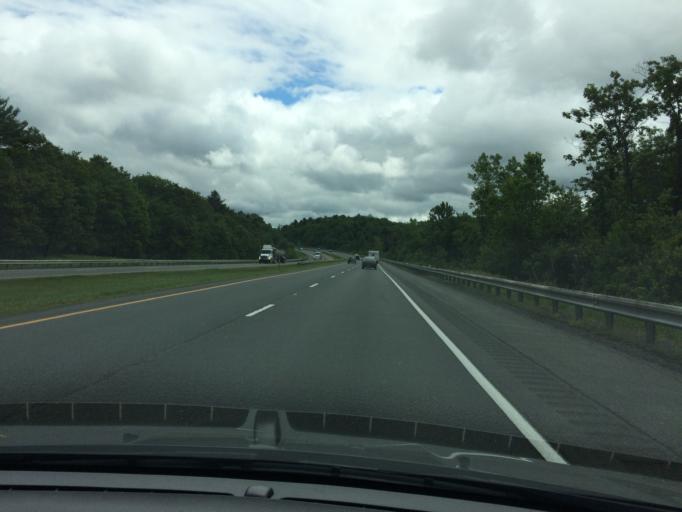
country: US
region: Massachusetts
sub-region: Berkshire County
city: Otis
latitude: 42.2355
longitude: -73.0517
